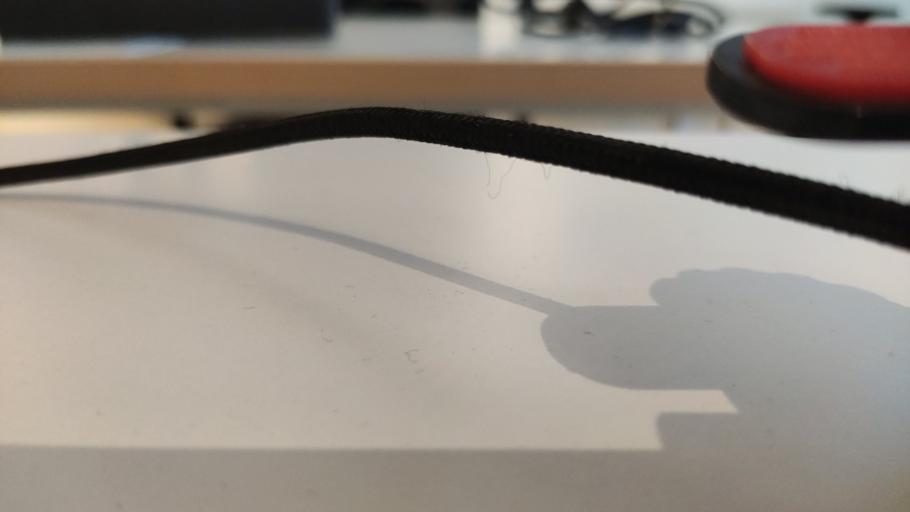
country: RU
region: Moskovskaya
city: Novopetrovskoye
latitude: 55.8712
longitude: 36.3998
